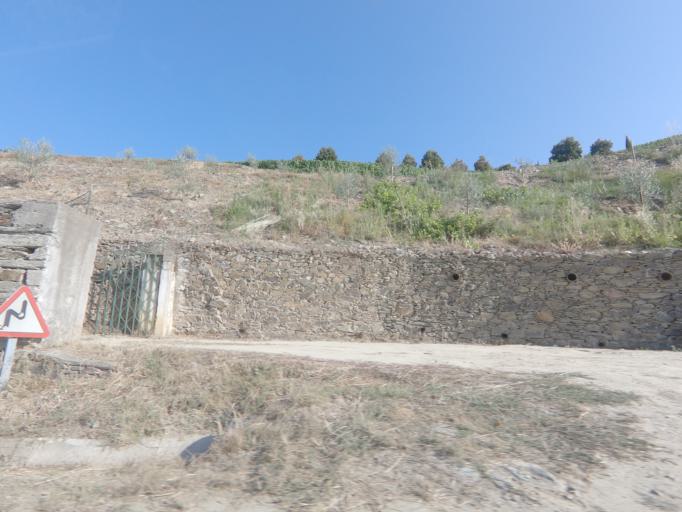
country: PT
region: Vila Real
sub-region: Sabrosa
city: Vilela
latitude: 41.2040
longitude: -7.5570
